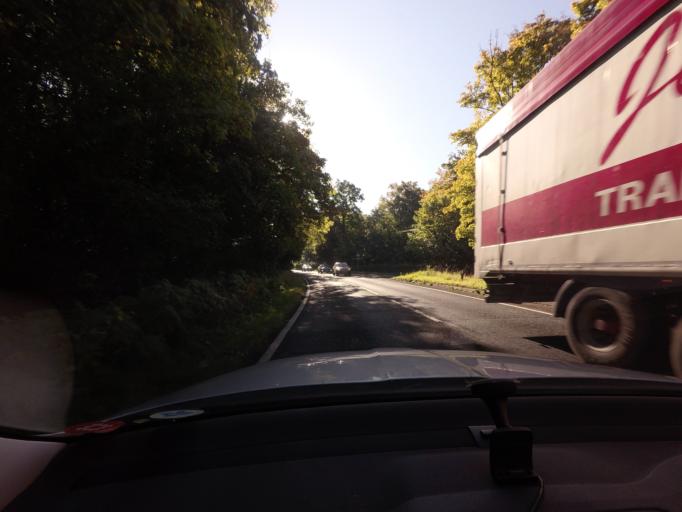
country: GB
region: England
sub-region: Kent
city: Tonbridge
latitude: 51.2385
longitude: 0.2792
